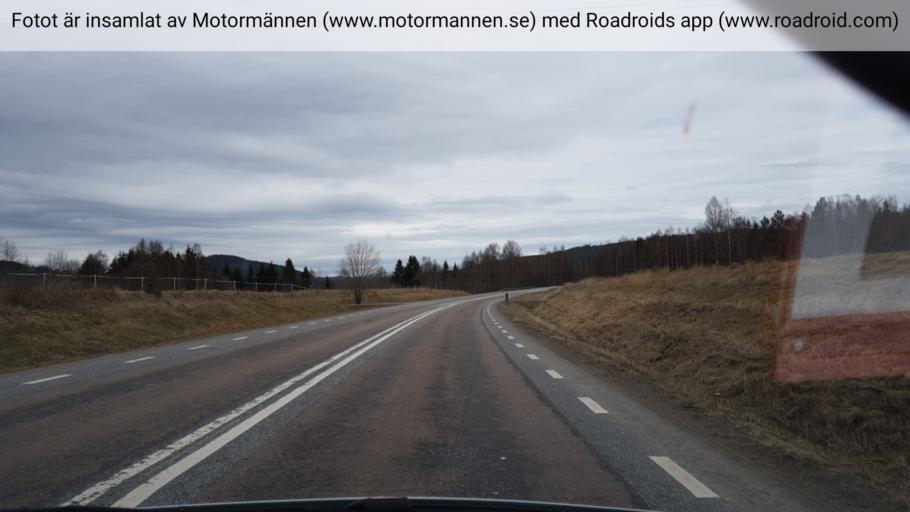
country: SE
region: Vaesternorrland
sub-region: Solleftea Kommun
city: Solleftea
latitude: 63.2735
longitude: 17.2101
